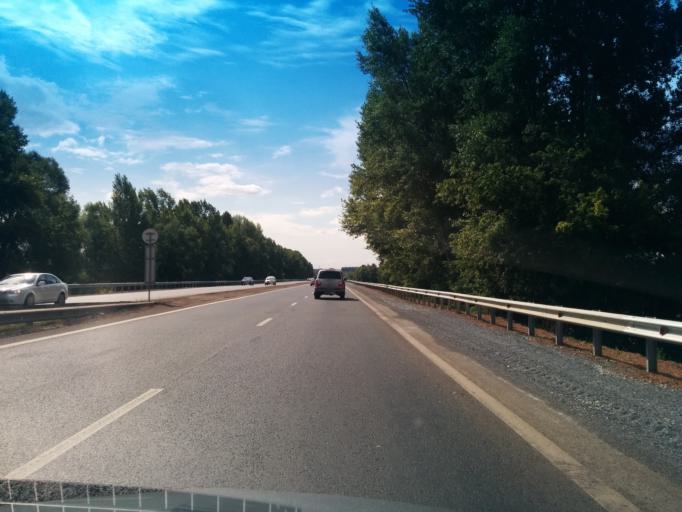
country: RU
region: Bashkortostan
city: Avdon
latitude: 54.5123
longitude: 55.8994
